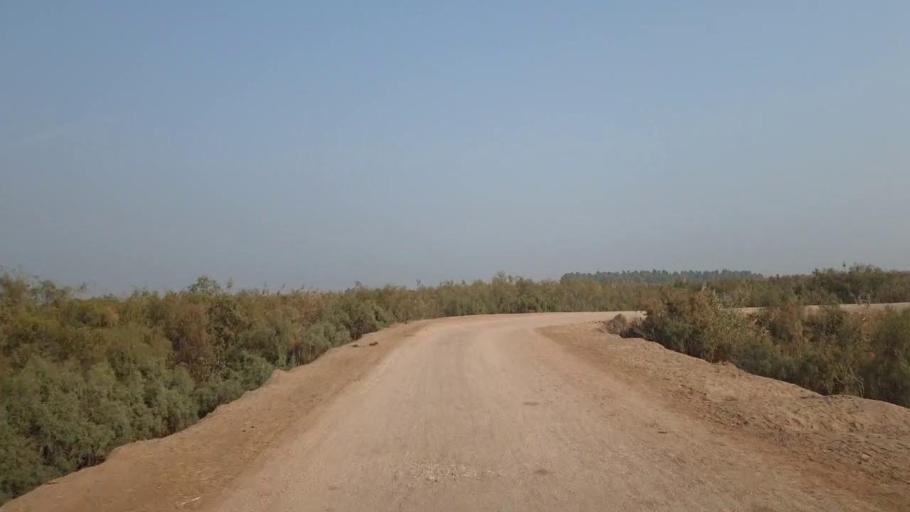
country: PK
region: Sindh
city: Shahdadpur
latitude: 25.9687
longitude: 68.5228
